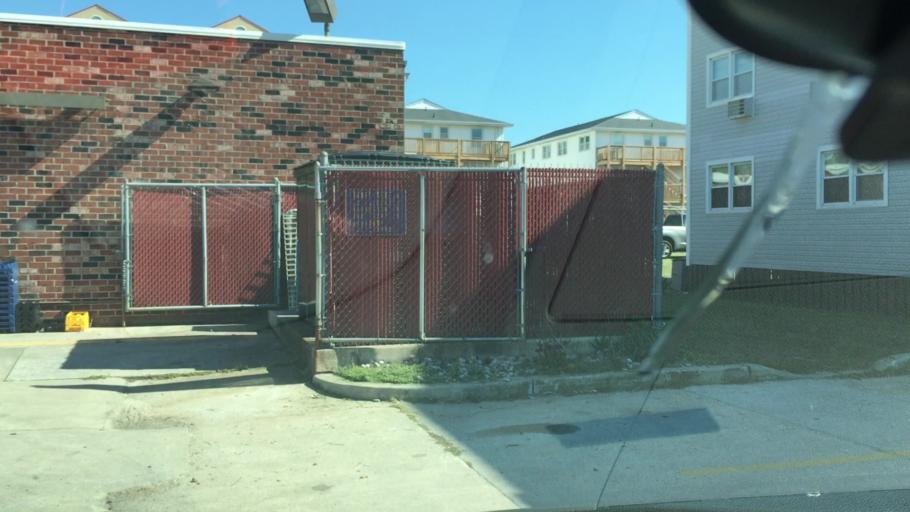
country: US
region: Delaware
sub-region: Sussex County
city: Bethany Beach
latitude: 38.4444
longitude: -75.0524
